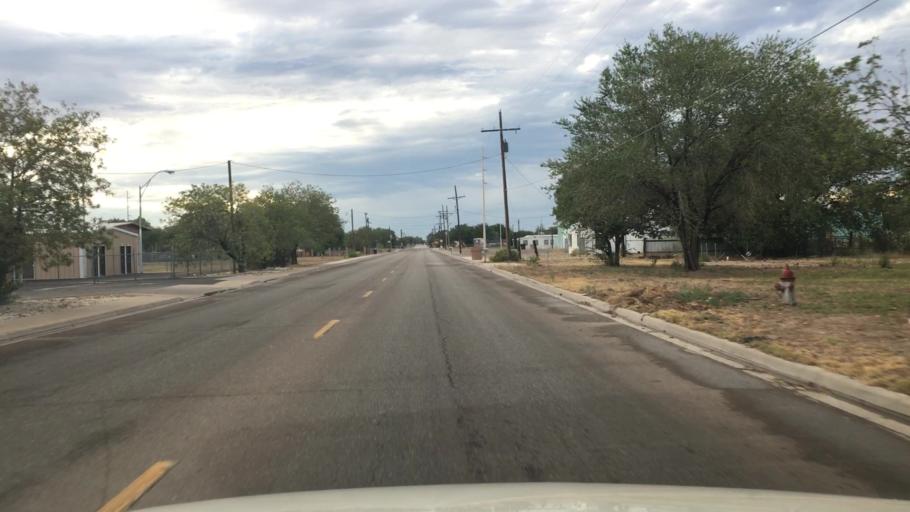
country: US
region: New Mexico
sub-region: Chaves County
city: Roswell
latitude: 33.4160
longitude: -104.5075
